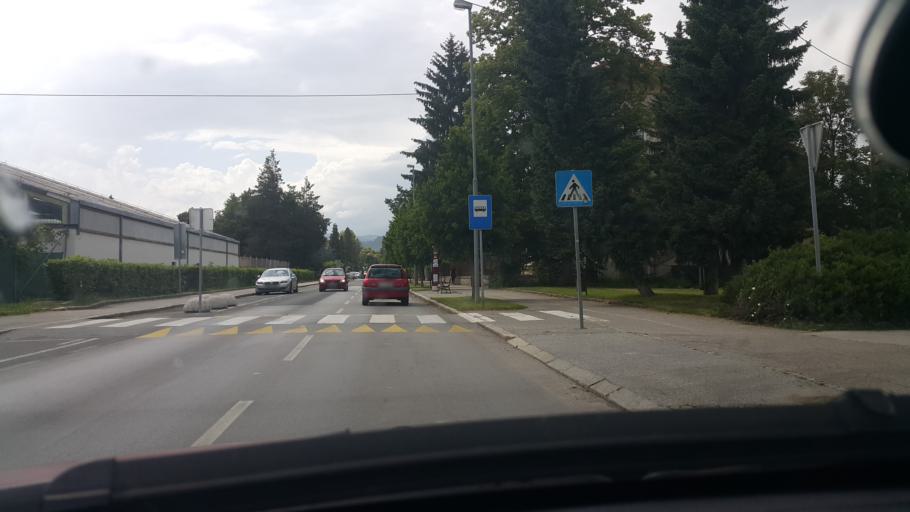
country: SI
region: Maribor
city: Maribor
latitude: 46.5639
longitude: 15.6396
